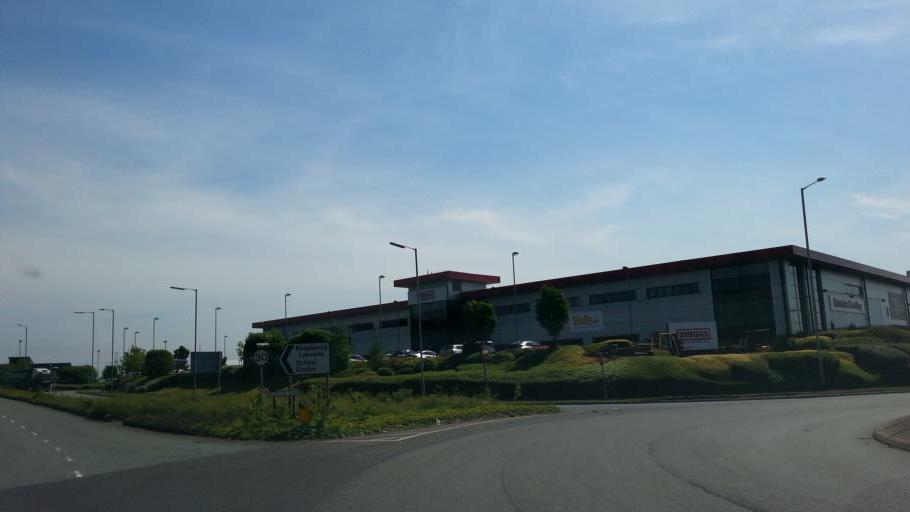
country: GB
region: England
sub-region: Staffordshire
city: Great Wyrley
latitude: 52.6780
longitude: -2.0187
